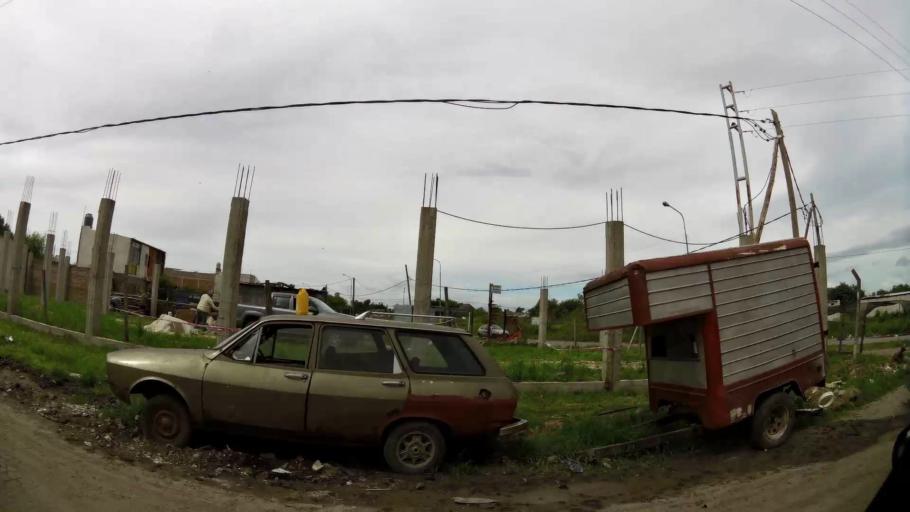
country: AR
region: Buenos Aires
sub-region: Partido de Quilmes
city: Quilmes
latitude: -34.7569
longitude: -58.2523
